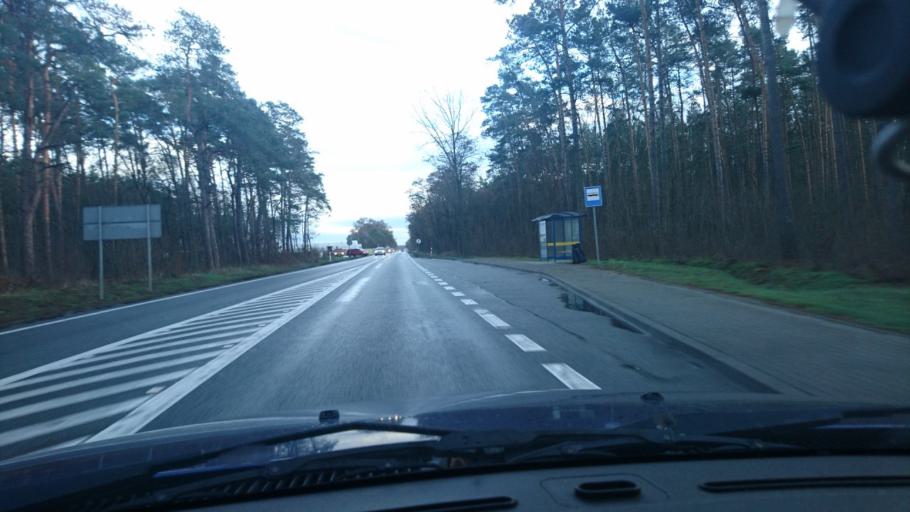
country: PL
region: Greater Poland Voivodeship
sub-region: Powiat kepinski
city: Kepno
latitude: 51.3252
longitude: 17.9660
